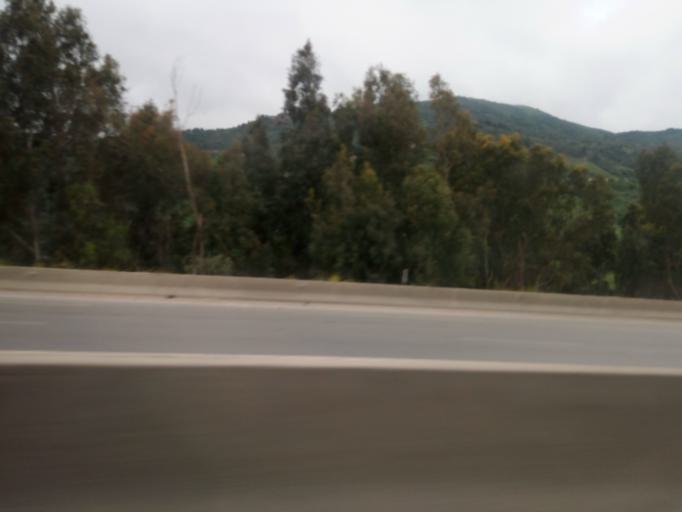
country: DZ
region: Bouira
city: Lakhdaria
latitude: 36.5556
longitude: 3.5802
